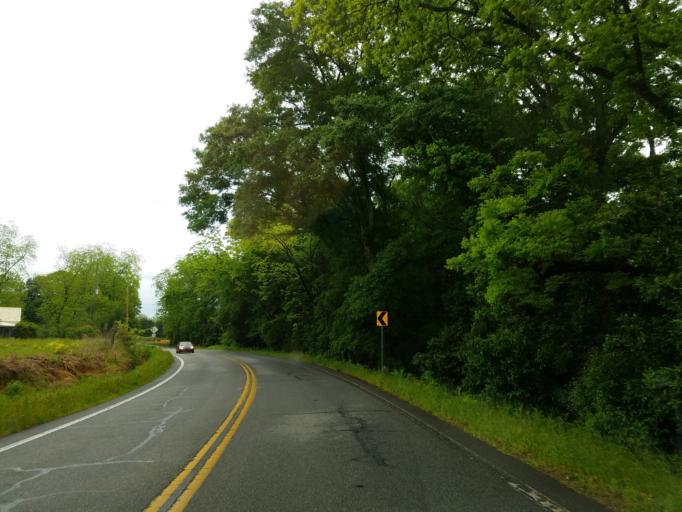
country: US
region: Georgia
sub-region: Peach County
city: Byron
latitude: 32.6520
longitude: -83.8022
